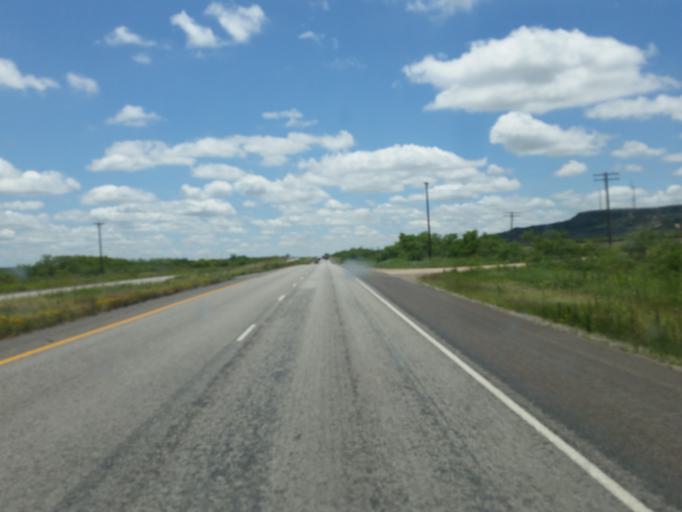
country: US
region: Texas
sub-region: Scurry County
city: Snyder
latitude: 32.9745
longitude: -101.1015
